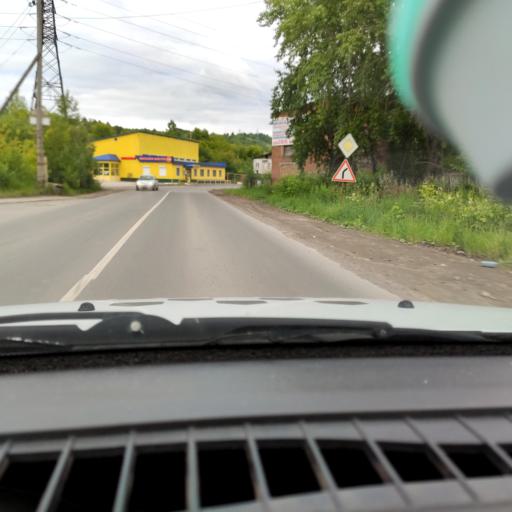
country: RU
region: Perm
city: Chusovoy
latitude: 58.3018
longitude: 57.8085
